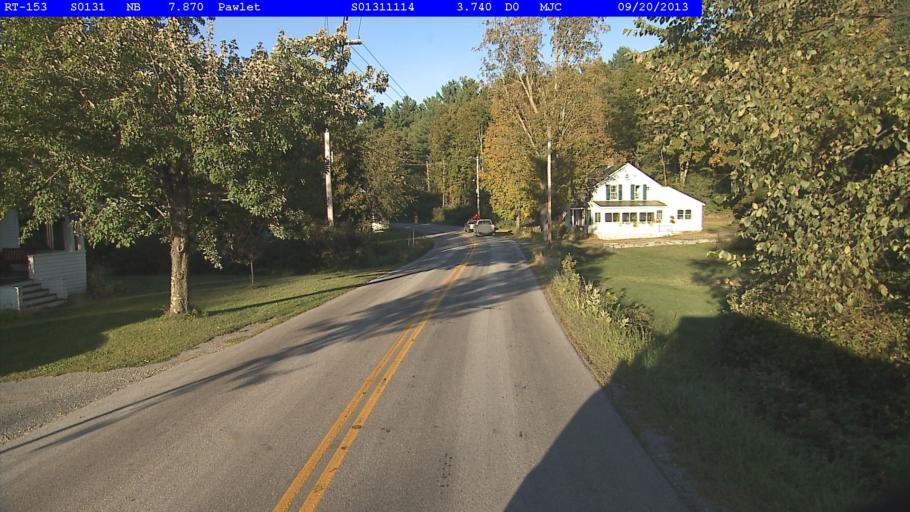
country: US
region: New York
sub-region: Washington County
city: Granville
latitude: 43.3623
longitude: -73.2411
